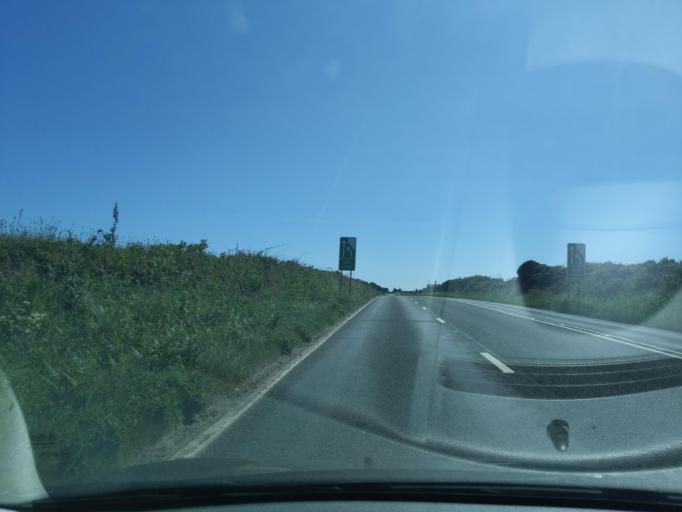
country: GB
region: England
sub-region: Cornwall
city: Wendron
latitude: 50.1431
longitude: -5.2150
